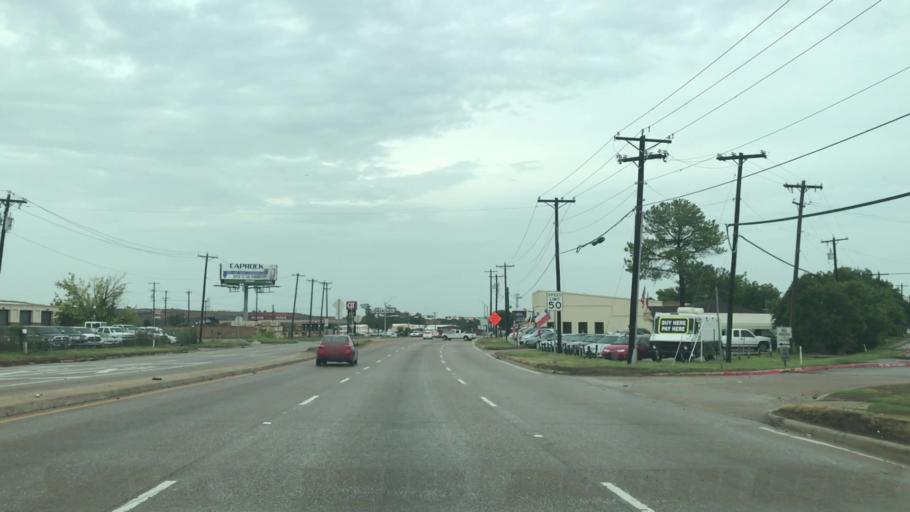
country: US
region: Texas
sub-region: Denton County
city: Lewisville
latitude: 33.0419
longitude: -96.9833
